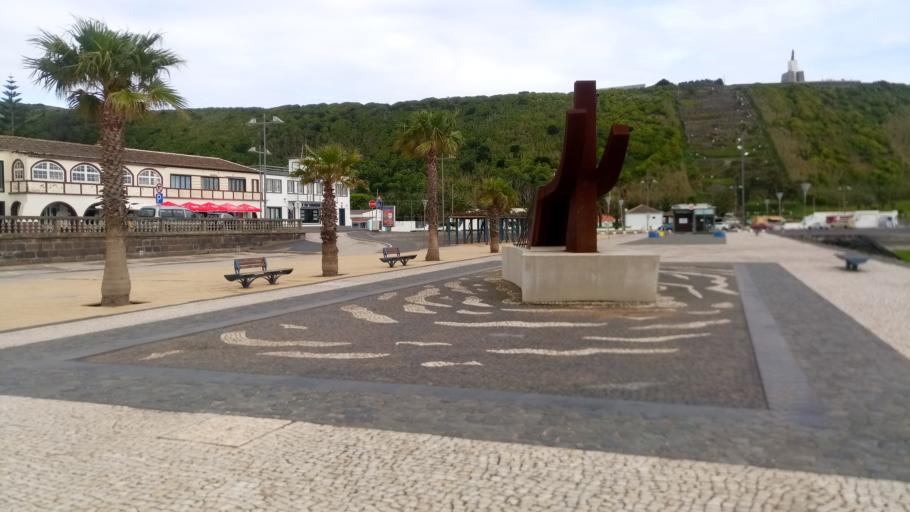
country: PT
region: Azores
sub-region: Praia da Vitoria
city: Praia da Vitoria
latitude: 38.7317
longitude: -27.0580
